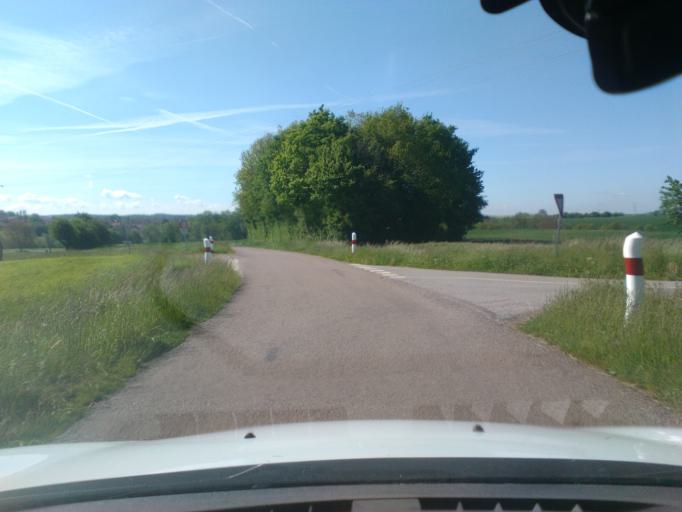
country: FR
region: Lorraine
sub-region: Departement des Vosges
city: Mirecourt
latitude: 48.3077
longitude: 6.1672
